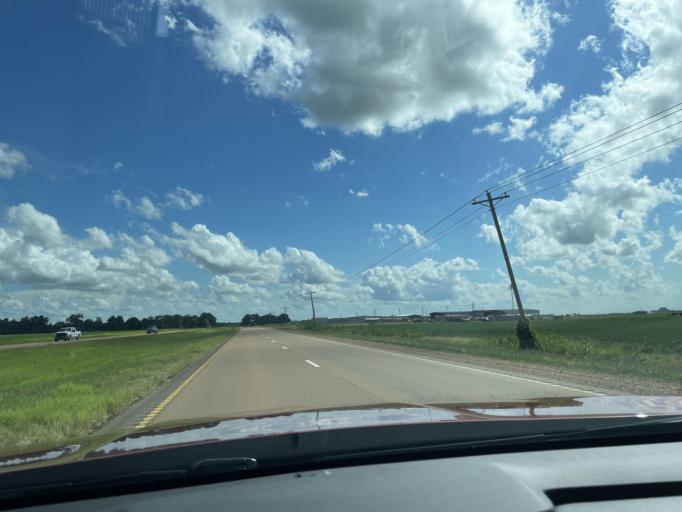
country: US
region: Mississippi
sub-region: Humphreys County
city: Belzoni
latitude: 33.1466
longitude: -90.5106
